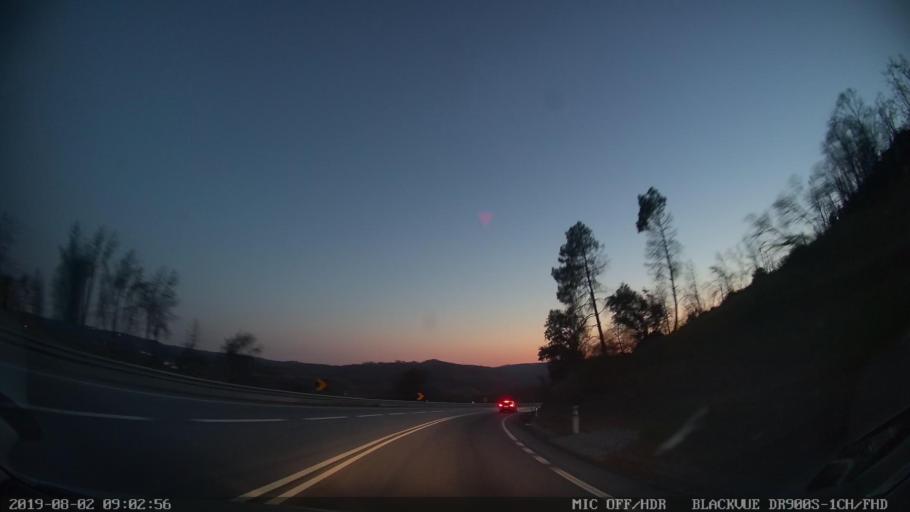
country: PT
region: Portalegre
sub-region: Nisa
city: Nisa
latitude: 39.5505
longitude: -7.7943
